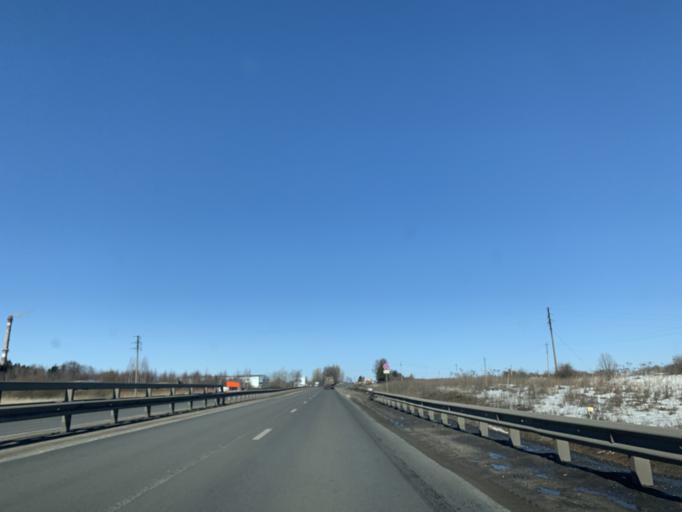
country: RU
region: Jaroslavl
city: Konstantinovskiy
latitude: 57.8422
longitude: 39.5513
